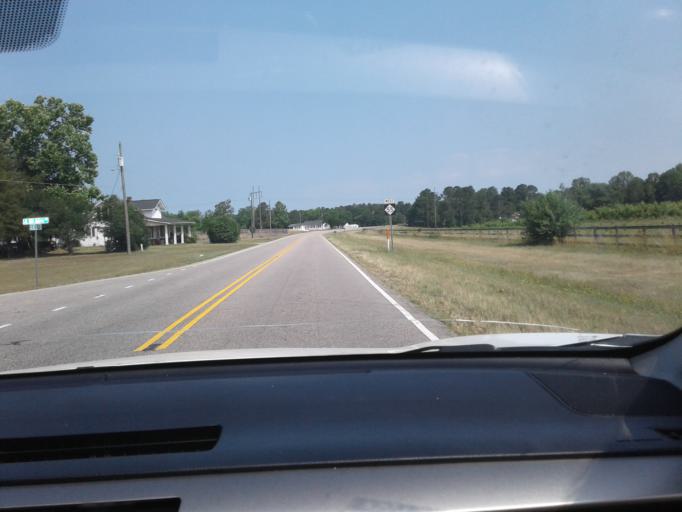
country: US
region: North Carolina
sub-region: Harnett County
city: Coats
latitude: 35.4527
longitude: -78.6879
